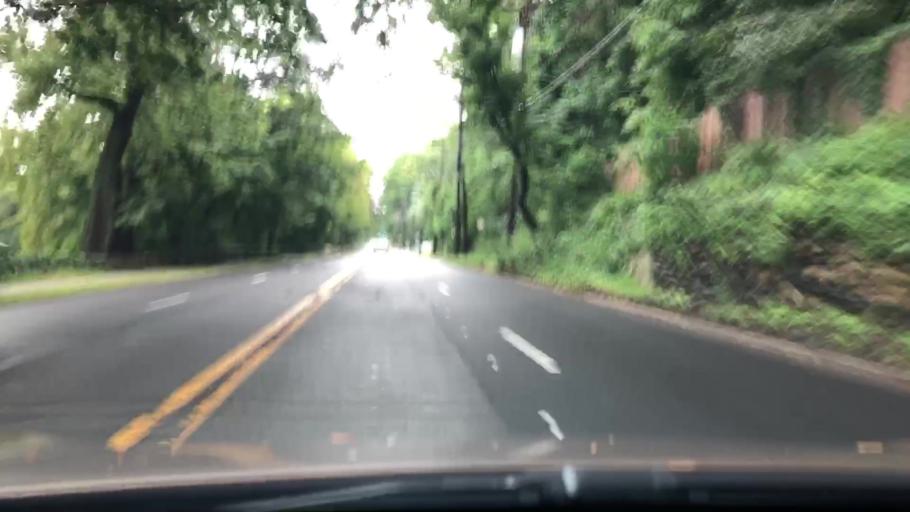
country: US
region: New York
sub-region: Westchester County
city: Scarsdale
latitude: 40.9951
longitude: -73.7911
